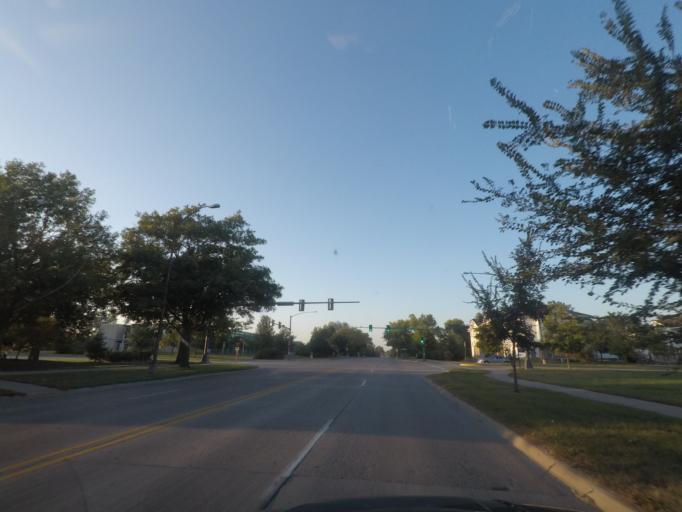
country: US
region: Iowa
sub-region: Story County
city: Ames
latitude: 42.0334
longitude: -93.6447
